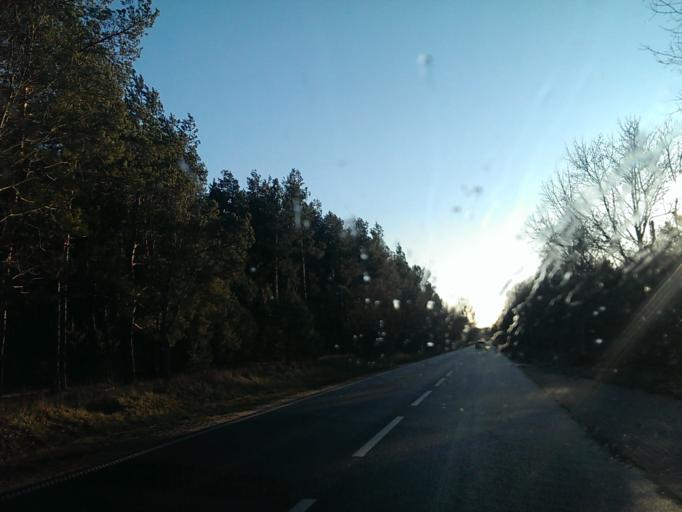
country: PL
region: Kujawsko-Pomorskie
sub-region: Powiat nakielski
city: Naklo nad Notecia
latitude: 53.0826
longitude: 17.5872
